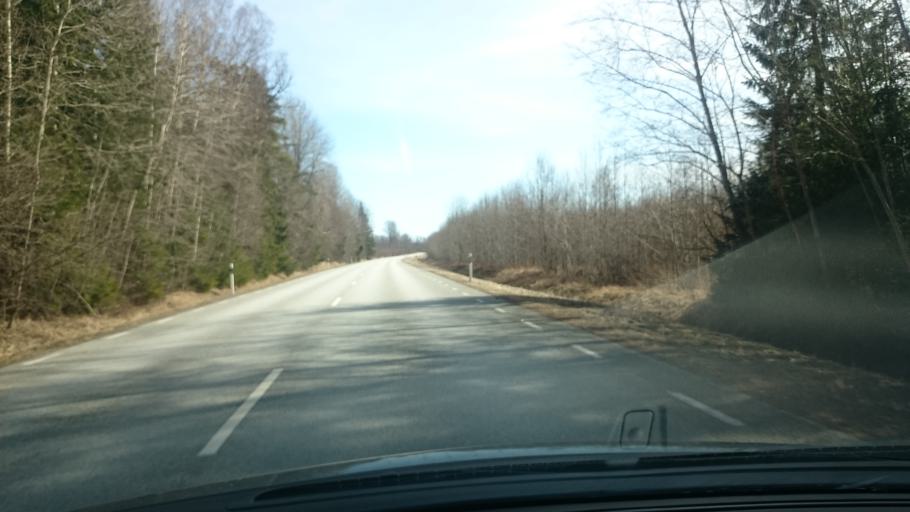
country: EE
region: Paernumaa
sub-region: Tootsi vald
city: Tootsi
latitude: 58.6623
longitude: 24.8190
